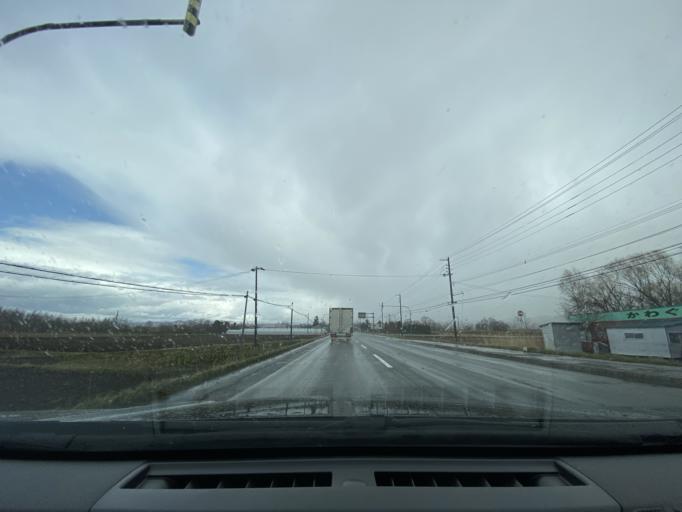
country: JP
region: Hokkaido
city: Fukagawa
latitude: 43.6778
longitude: 142.0310
